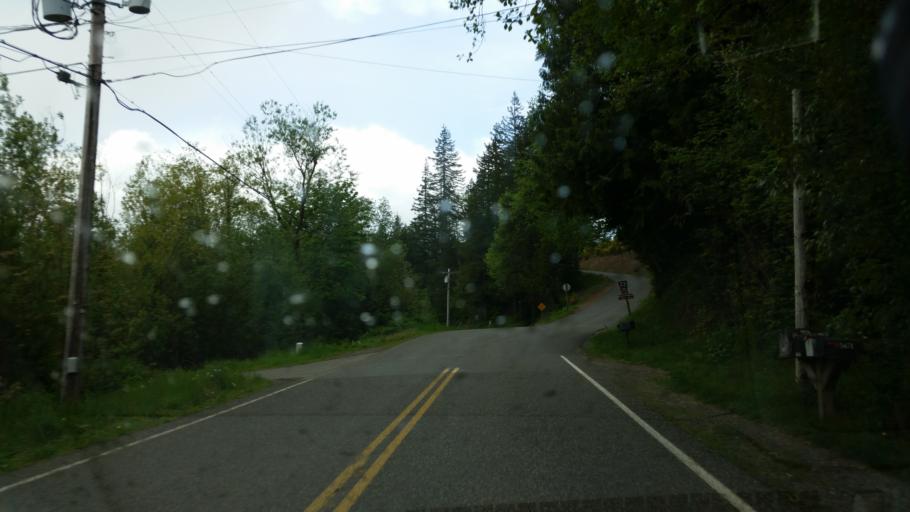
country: US
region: Washington
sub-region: Mason County
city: Shelton
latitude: 47.3226
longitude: -123.2718
